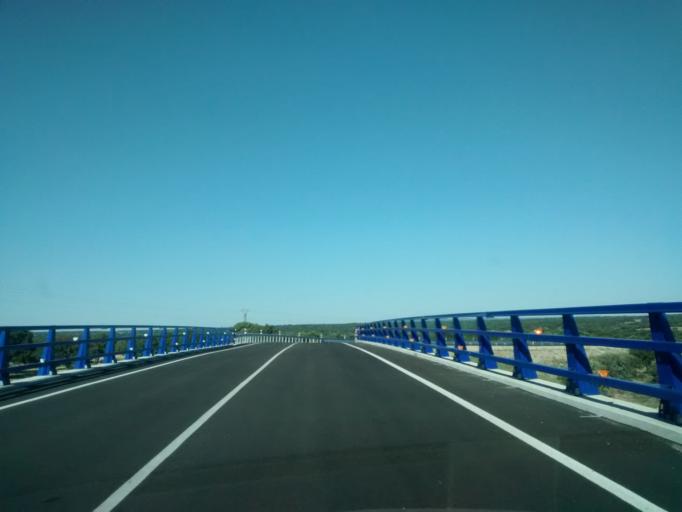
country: ES
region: Castille and Leon
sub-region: Provincia de Salamanca
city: Fuentes de Onoro
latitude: 40.5911
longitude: -6.7849
